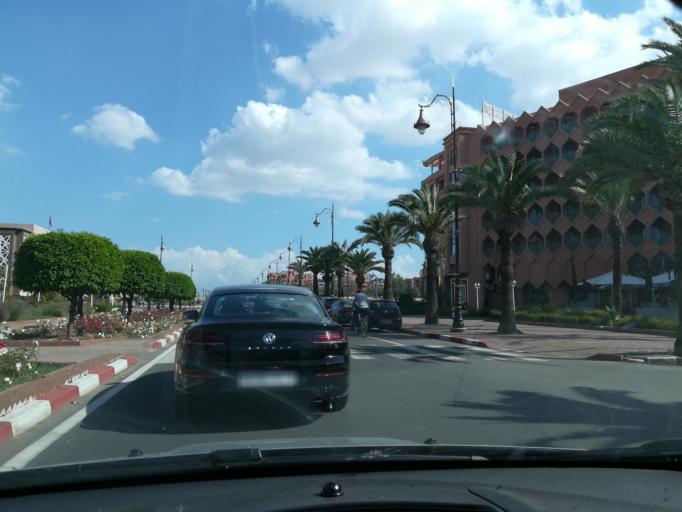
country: MA
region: Marrakech-Tensift-Al Haouz
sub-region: Marrakech
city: Marrakesh
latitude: 31.6232
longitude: -8.0117
